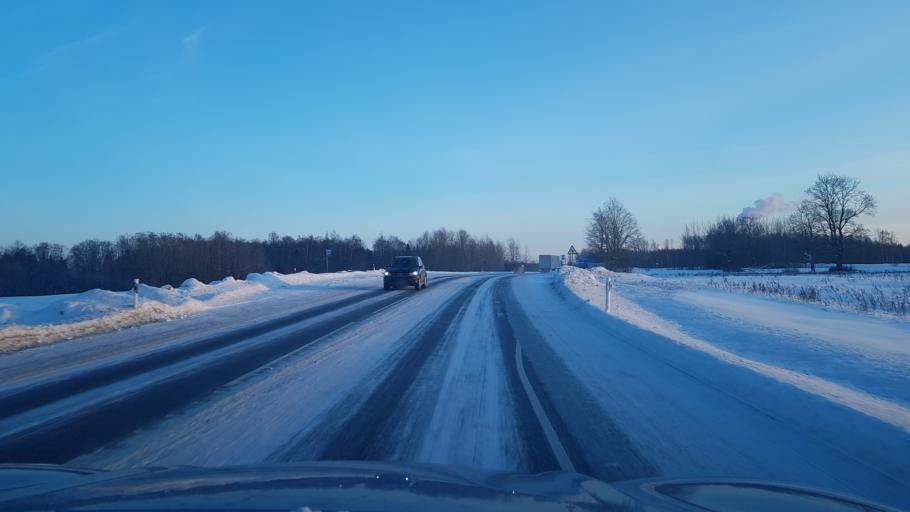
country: EE
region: Ida-Virumaa
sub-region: Narva-Joesuu linn
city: Narva-Joesuu
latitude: 59.3976
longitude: 28.0763
